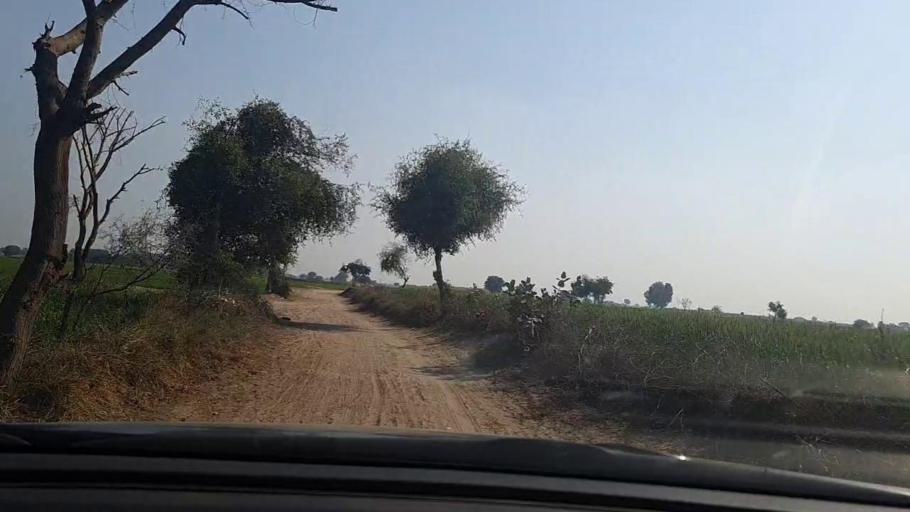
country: PK
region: Sindh
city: Sann
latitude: 26.2646
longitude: 68.0737
